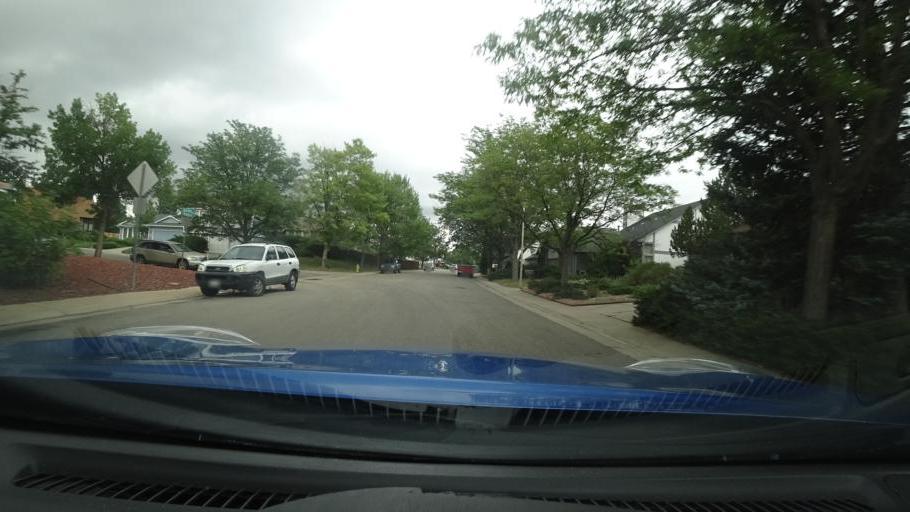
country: US
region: Colorado
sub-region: Adams County
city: Aurora
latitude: 39.7014
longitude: -104.8180
